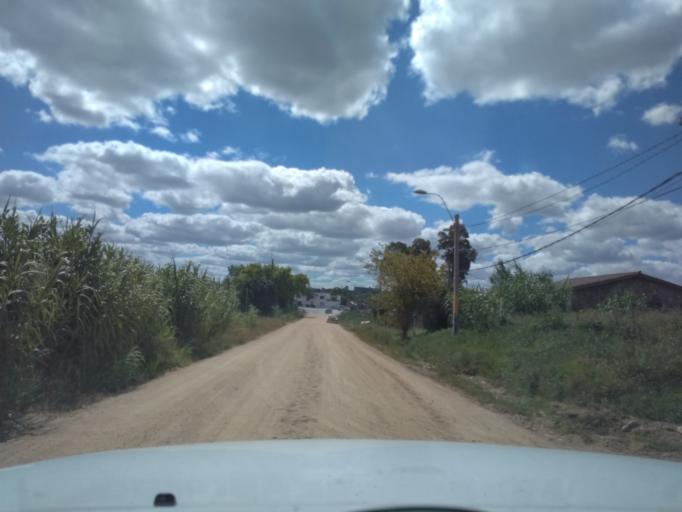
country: UY
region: Canelones
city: Colonia Nicolich
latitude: -34.8259
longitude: -55.9954
